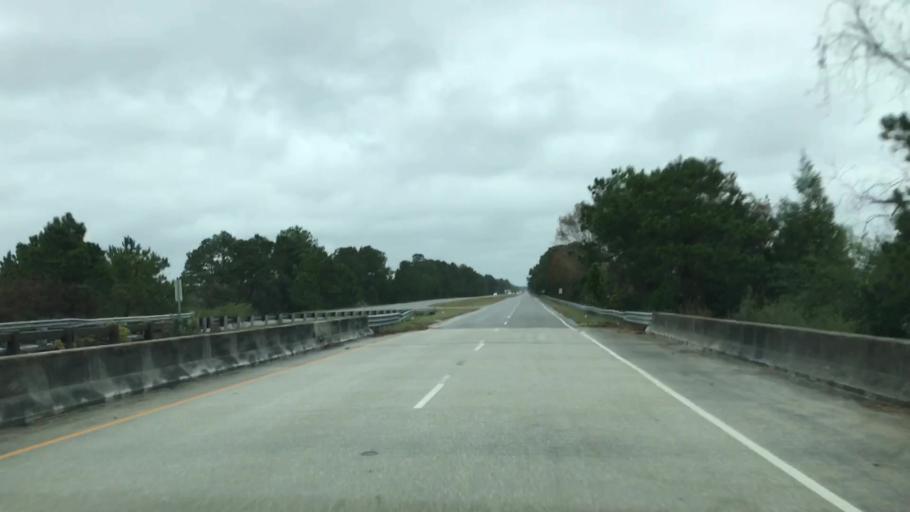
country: US
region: South Carolina
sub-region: Georgetown County
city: Georgetown
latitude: 33.1873
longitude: -79.4028
